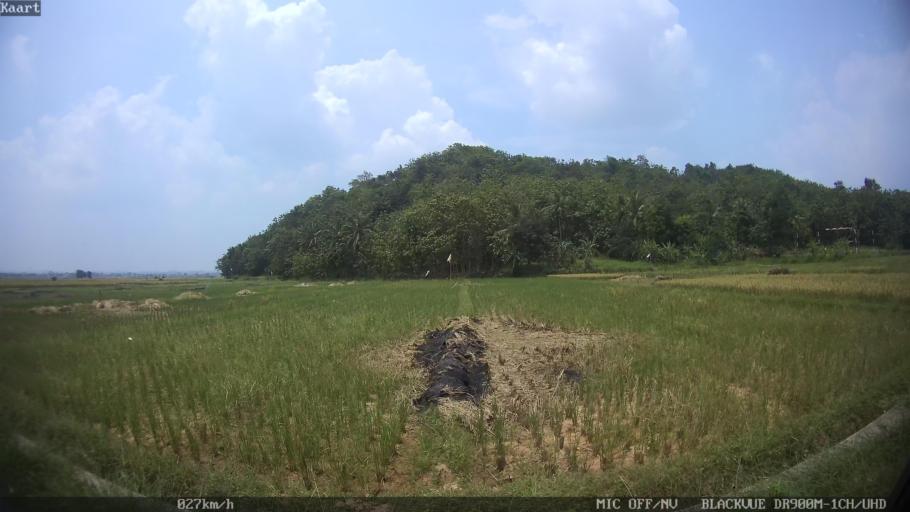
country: ID
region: Lampung
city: Pringsewu
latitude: -5.3819
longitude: 105.0065
